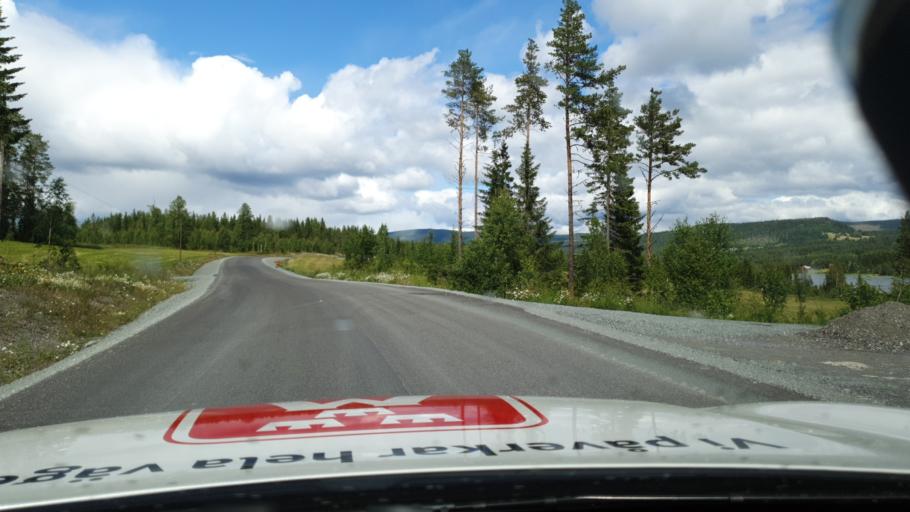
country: SE
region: Jaemtland
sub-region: Krokoms Kommun
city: Valla
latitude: 63.4410
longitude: 14.0605
